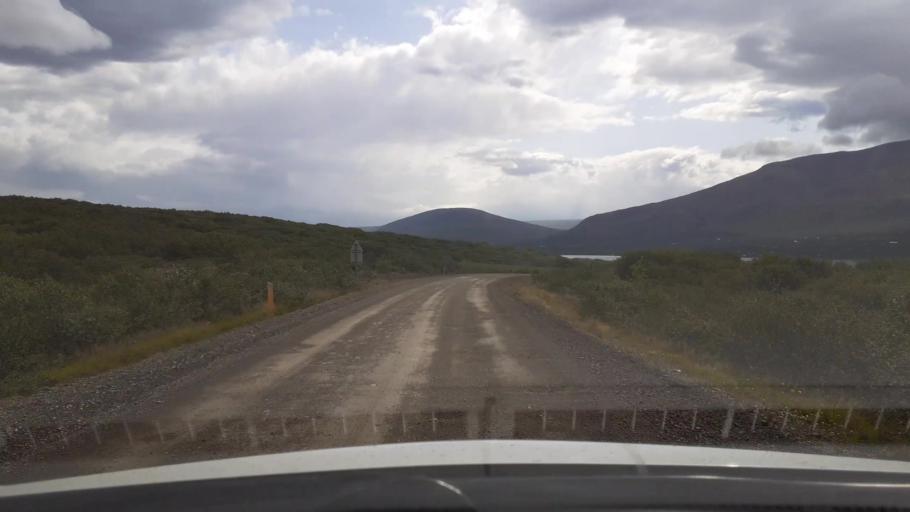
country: IS
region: West
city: Borgarnes
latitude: 64.5519
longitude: -21.6227
